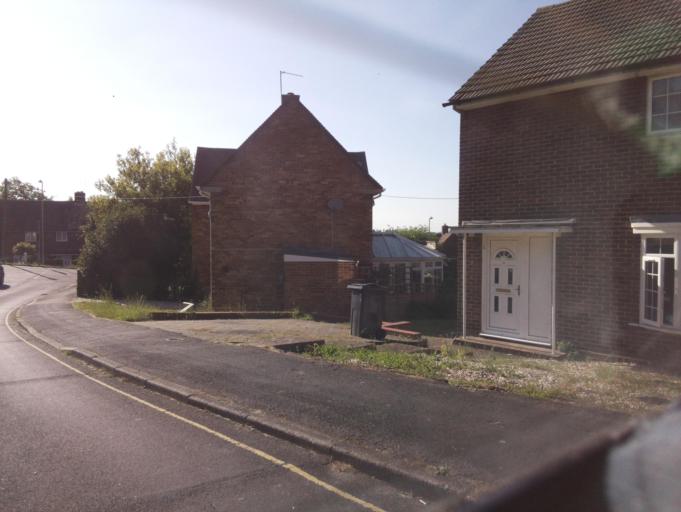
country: GB
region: England
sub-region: Hampshire
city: Winchester
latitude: 51.0642
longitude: -1.2978
